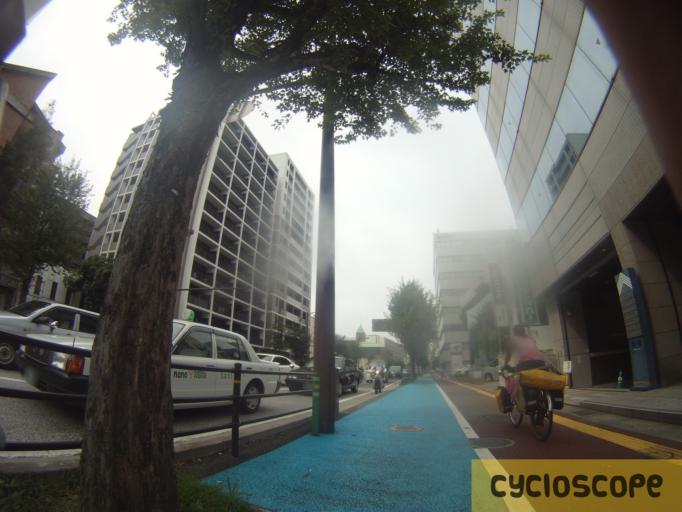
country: JP
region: Fukuoka
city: Fukuoka-shi
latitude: 33.5930
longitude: 130.3904
